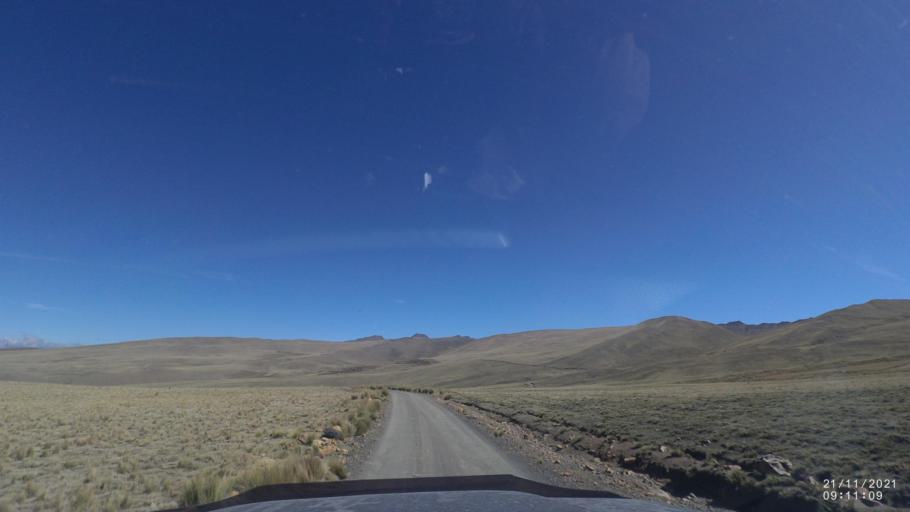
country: BO
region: Cochabamba
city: Cochabamba
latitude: -17.1490
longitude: -66.2581
